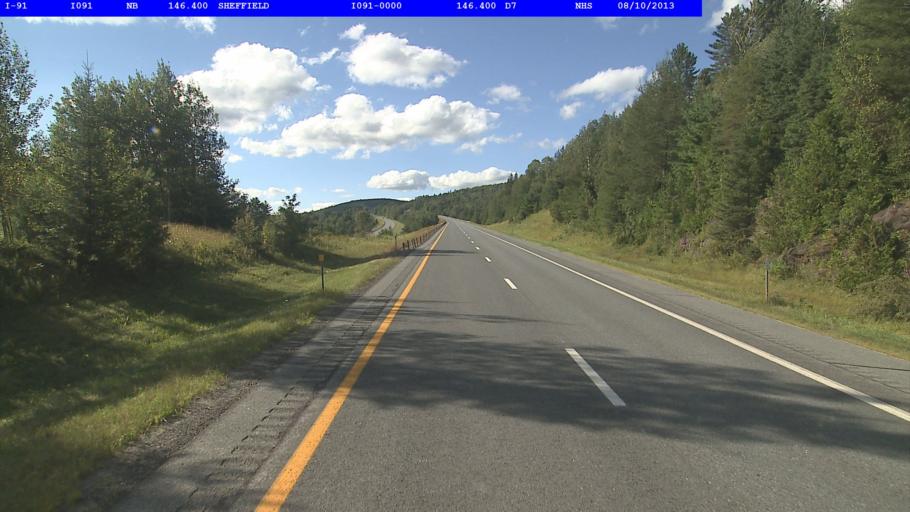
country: US
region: Vermont
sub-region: Caledonia County
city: Lyndonville
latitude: 44.6146
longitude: -72.1188
